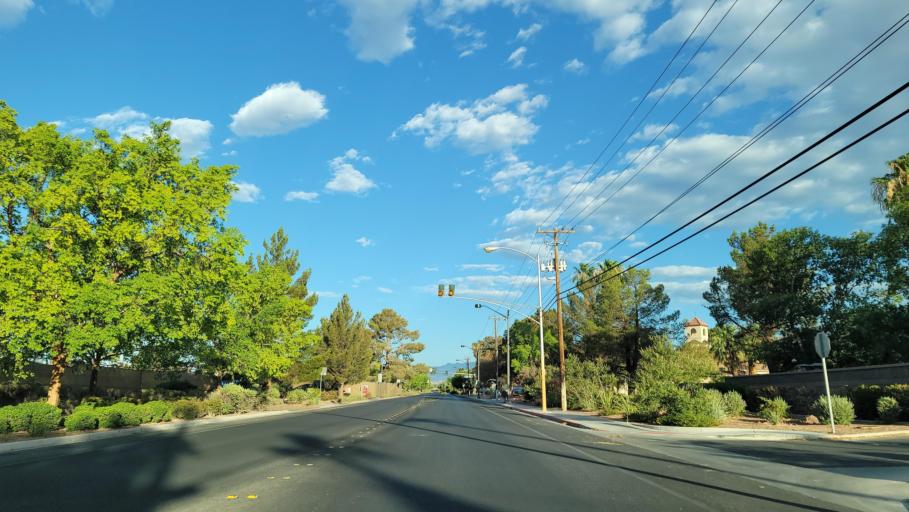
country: US
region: Nevada
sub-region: Clark County
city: Las Vegas
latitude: 36.1663
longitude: -115.1814
